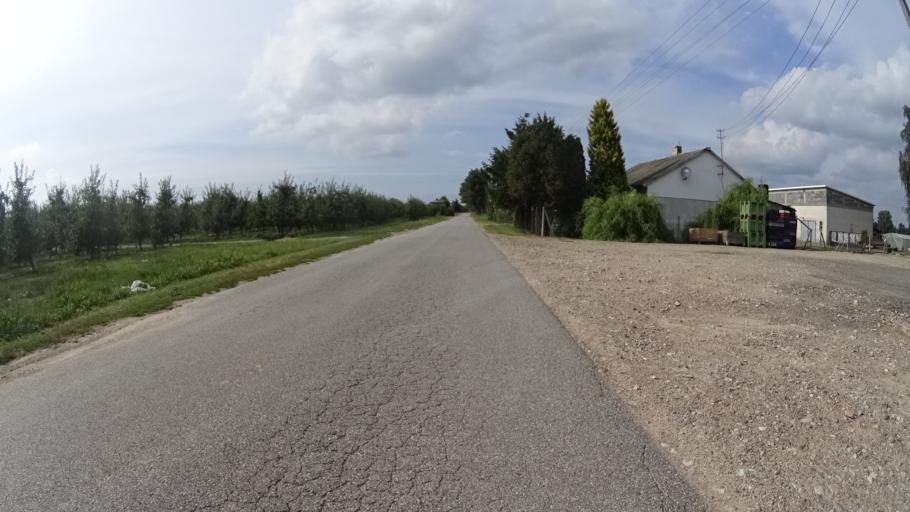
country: PL
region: Masovian Voivodeship
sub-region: Powiat grojecki
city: Goszczyn
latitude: 51.7034
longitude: 20.8454
